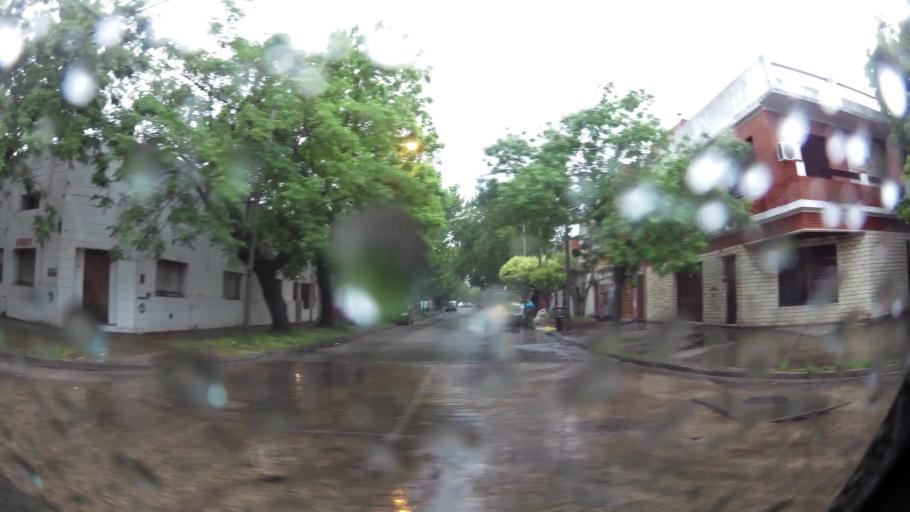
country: AR
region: Buenos Aires
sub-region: Partido de Lanus
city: Lanus
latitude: -34.7046
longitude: -58.4052
